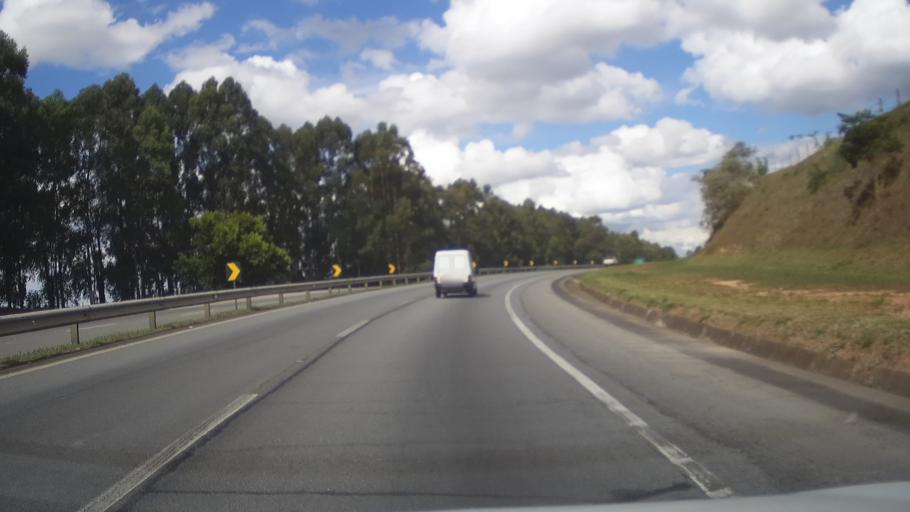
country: BR
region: Minas Gerais
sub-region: Oliveira
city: Oliveira
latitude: -20.8296
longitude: -44.8170
